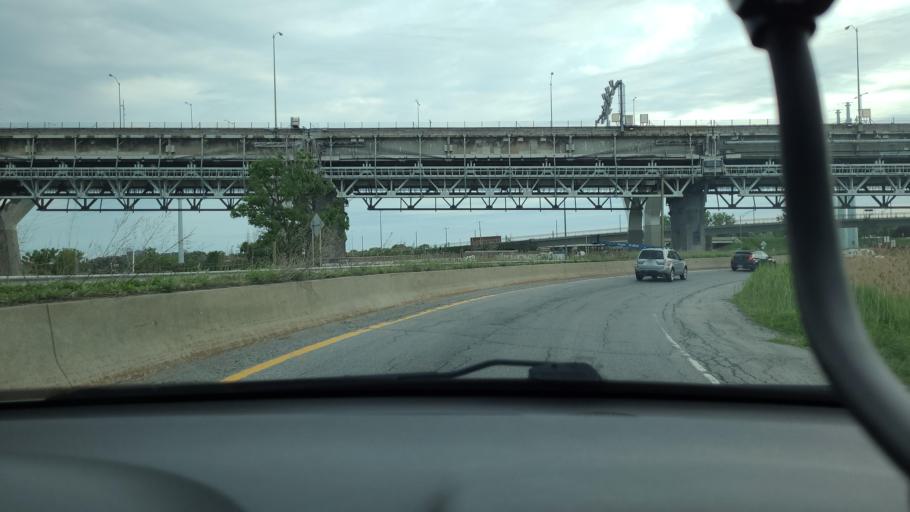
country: CA
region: Quebec
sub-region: Monteregie
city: Brossard
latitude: 45.4658
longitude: -73.4960
